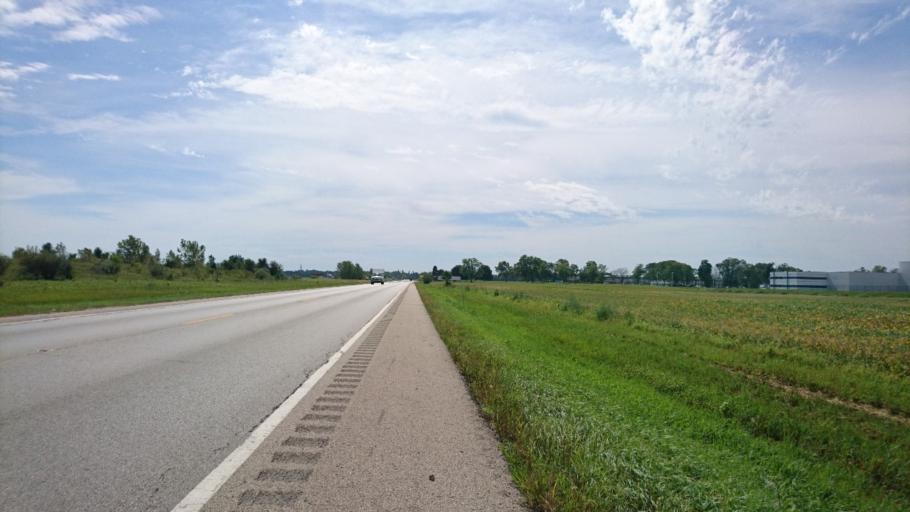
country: US
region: Illinois
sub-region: Will County
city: Wilmington
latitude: 41.3238
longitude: -88.1328
